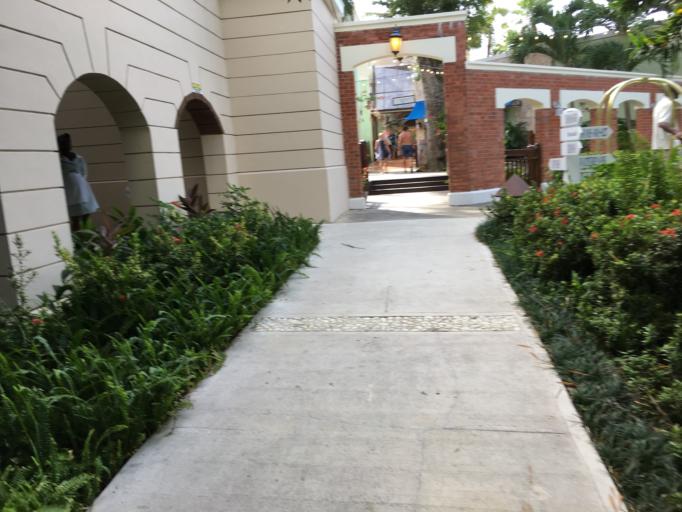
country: JM
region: Westmoreland
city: Negril
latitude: 18.3144
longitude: -78.3374
